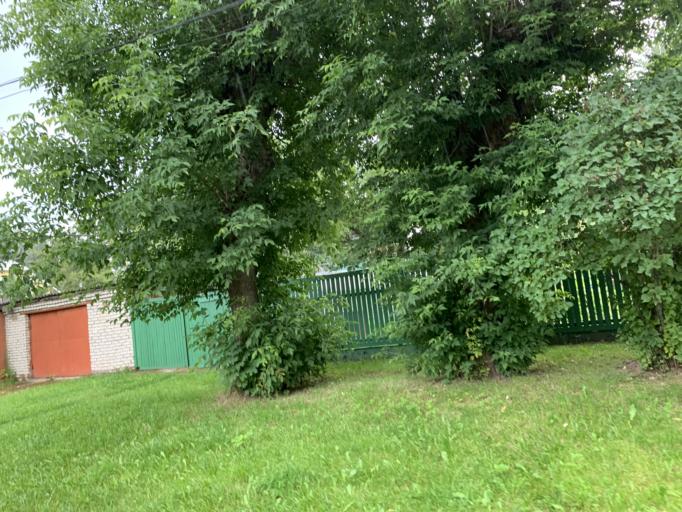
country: RU
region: Moskovskaya
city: Mamontovka
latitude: 55.9734
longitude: 37.8323
